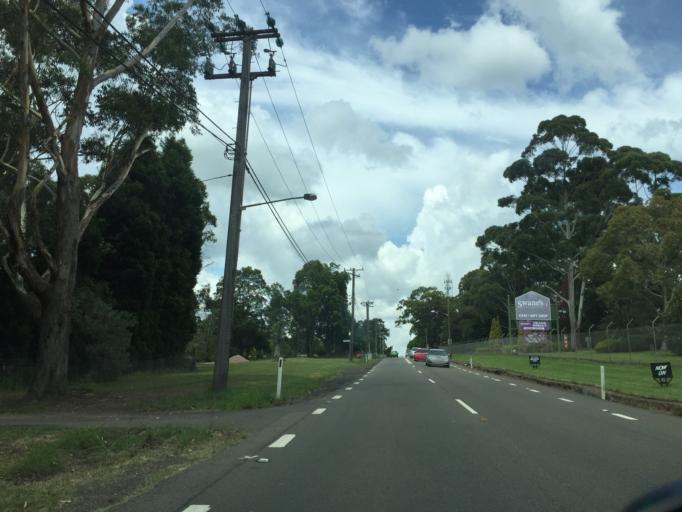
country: AU
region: New South Wales
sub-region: Hornsby Shire
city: Galston
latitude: -33.6744
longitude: 151.0337
